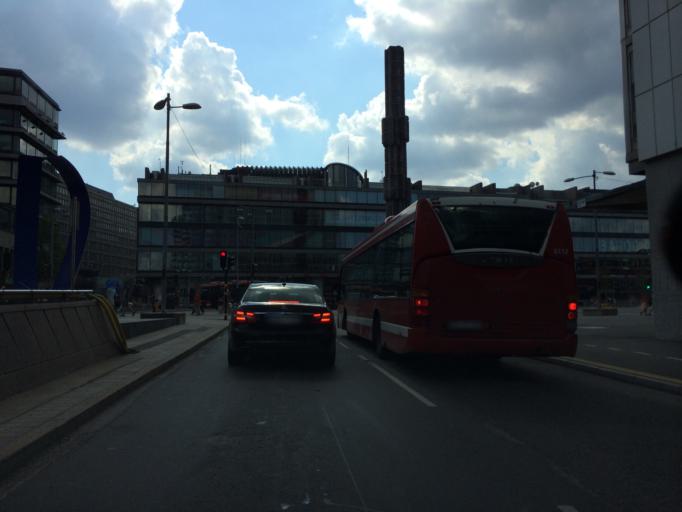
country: SE
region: Stockholm
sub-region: Stockholms Kommun
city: Stockholm
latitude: 59.3333
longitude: 18.0650
